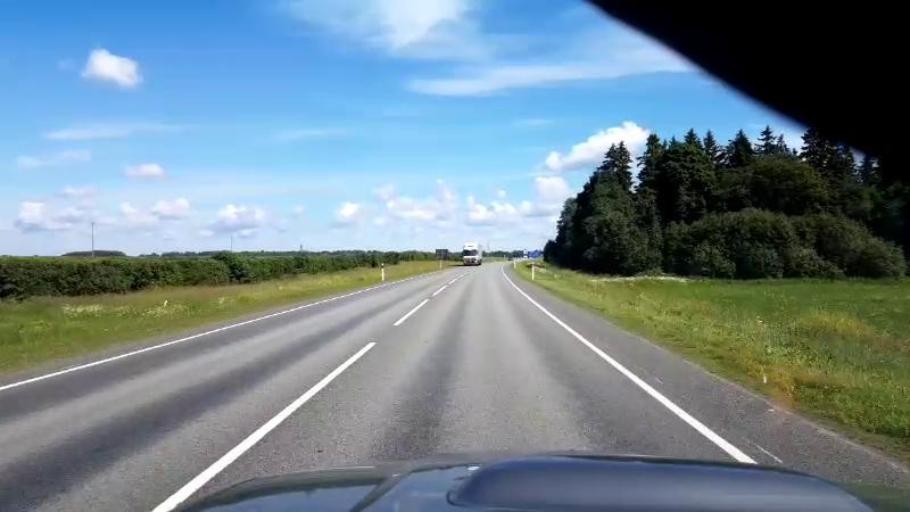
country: EE
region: Jaervamaa
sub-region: Jaerva-Jaani vald
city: Jarva-Jaani
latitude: 59.1744
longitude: 25.7581
